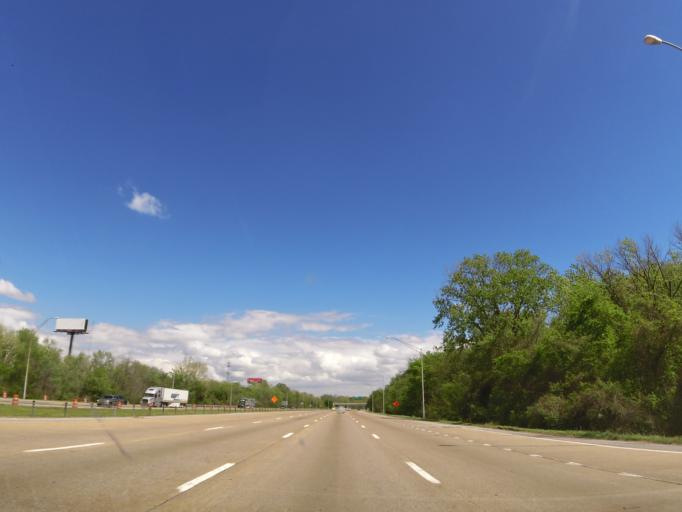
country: US
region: Tennessee
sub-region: Shelby County
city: Memphis
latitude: 35.1923
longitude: -90.0014
